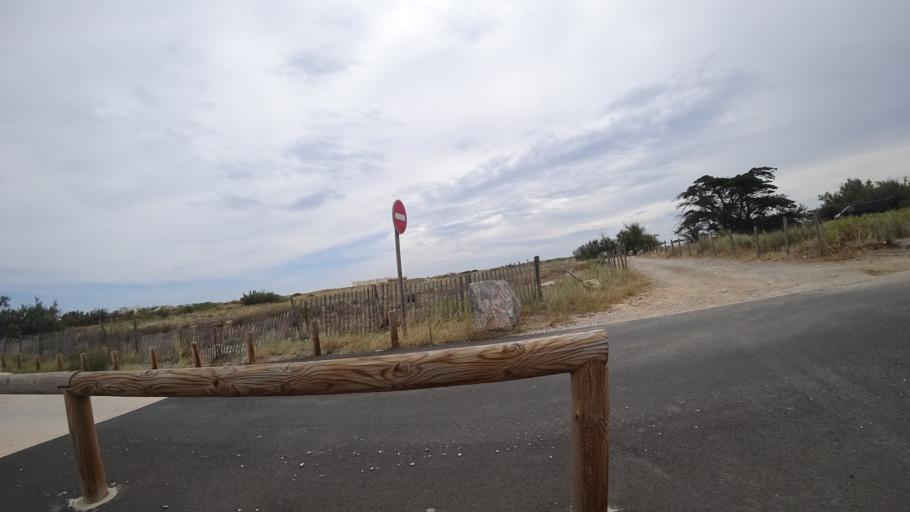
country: FR
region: Languedoc-Roussillon
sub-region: Departement de l'Aude
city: Leucate
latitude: 42.8984
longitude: 3.0522
